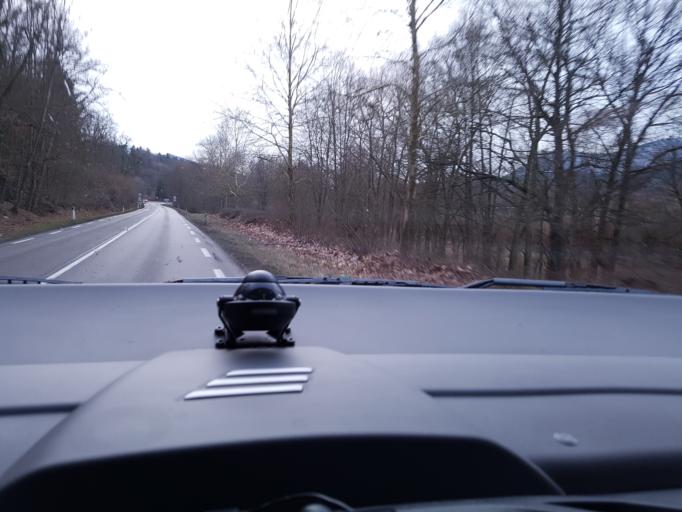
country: FR
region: Alsace
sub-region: Departement du Bas-Rhin
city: Chatenois
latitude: 48.2795
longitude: 7.3540
